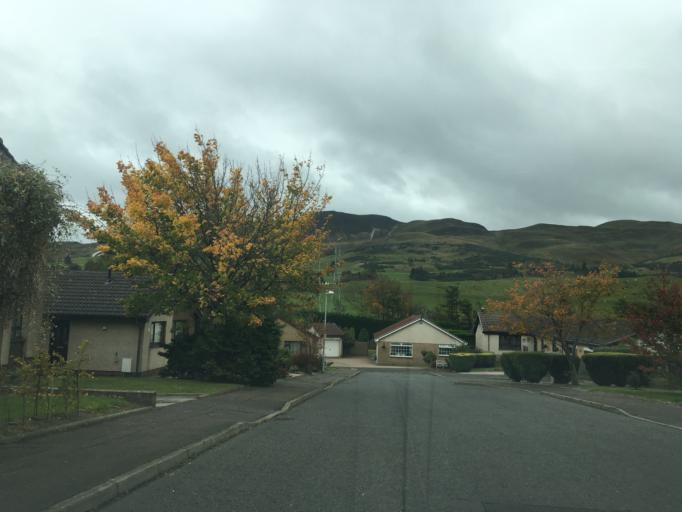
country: GB
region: Scotland
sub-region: Edinburgh
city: Colinton
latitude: 55.9000
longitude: -3.2215
